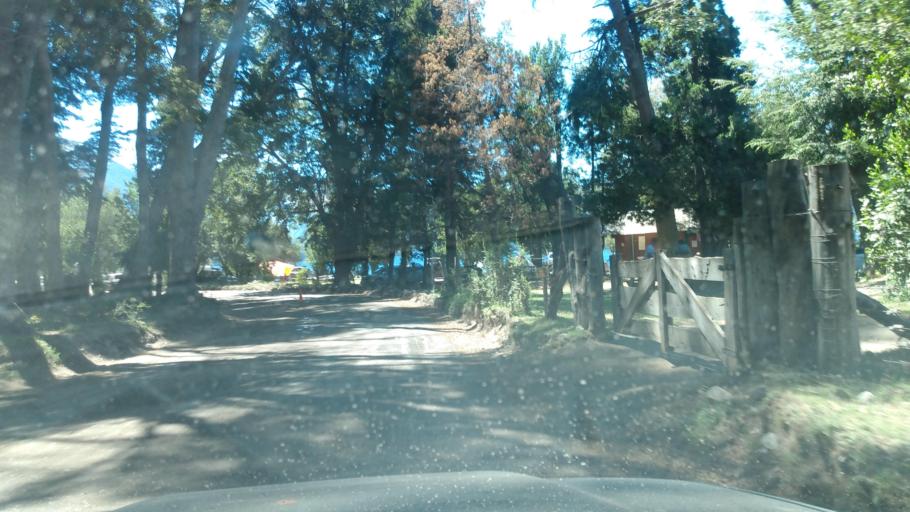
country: AR
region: Neuquen
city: Villa La Angostura
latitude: -40.6276
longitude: -71.4940
